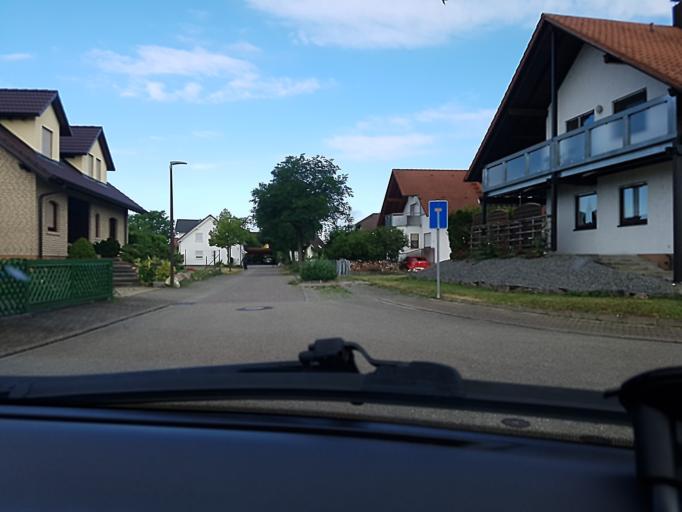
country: DE
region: Baden-Wuerttemberg
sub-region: Freiburg Region
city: Willstatt
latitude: 48.5183
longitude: 7.8872
